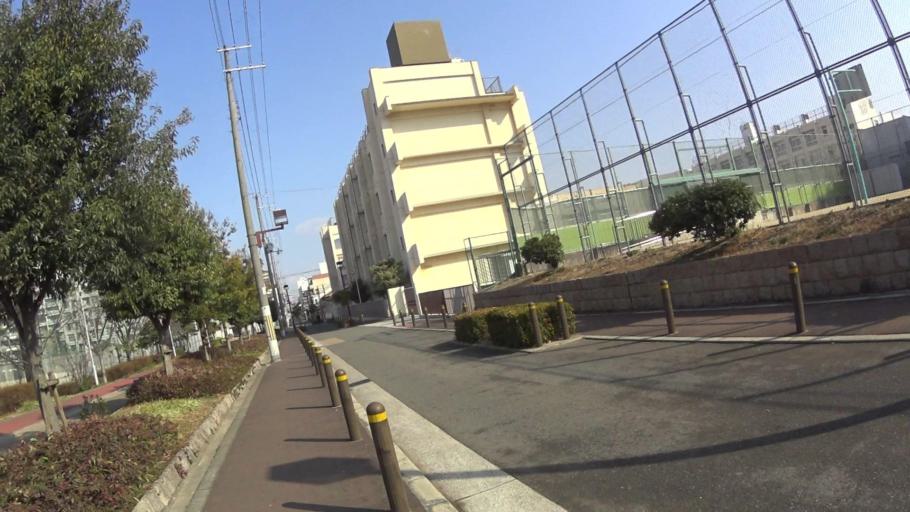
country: JP
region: Osaka
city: Sakai
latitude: 34.6040
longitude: 135.5026
